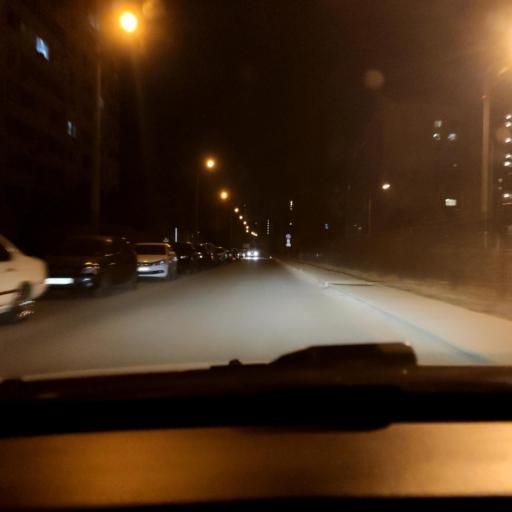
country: RU
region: Voronezj
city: Voronezh
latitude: 51.7097
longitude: 39.1870
